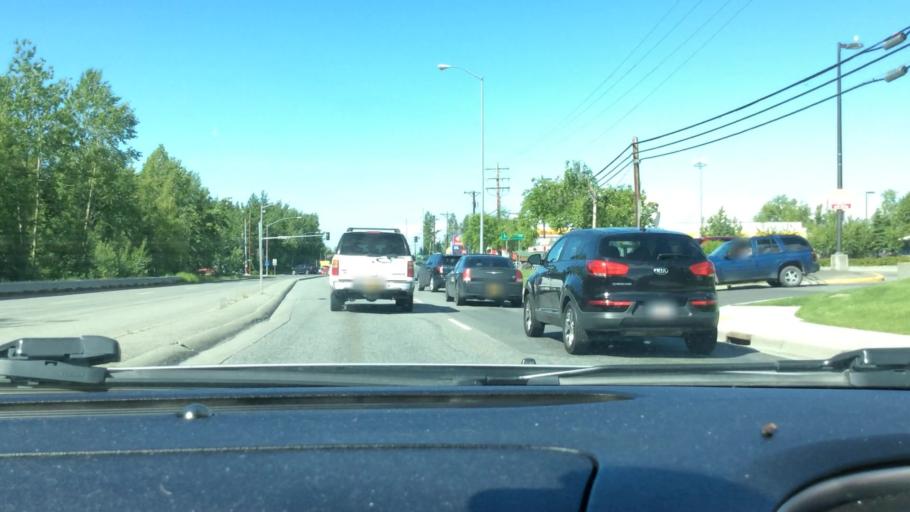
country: US
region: Alaska
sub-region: Anchorage Municipality
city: Anchorage
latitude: 61.2082
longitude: -149.7784
